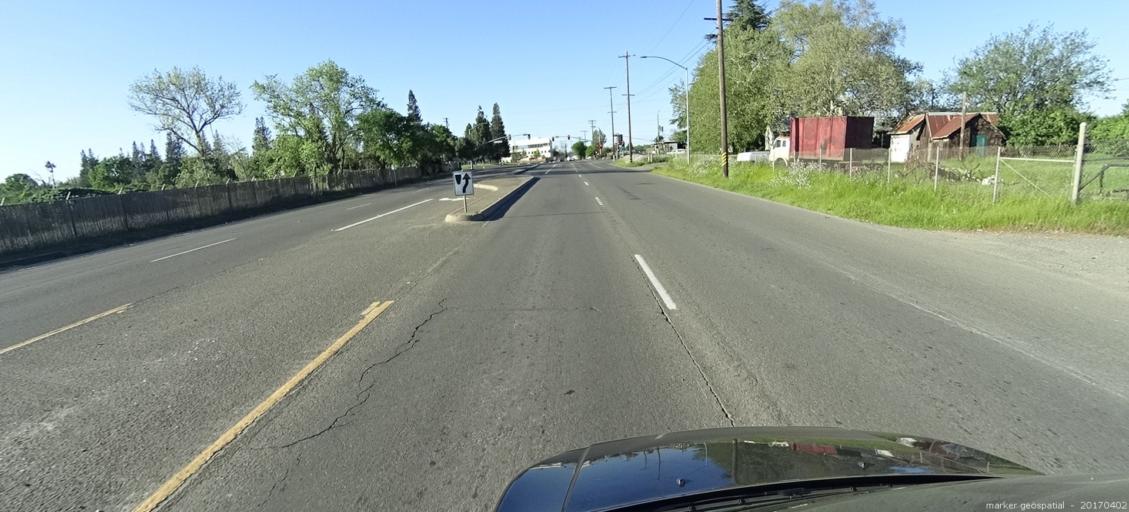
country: US
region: California
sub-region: Sacramento County
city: Rosemont
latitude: 38.5430
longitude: -121.3908
